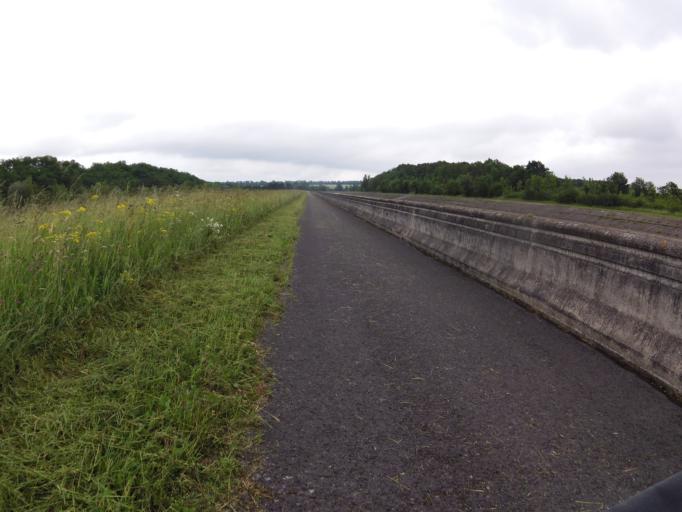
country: FR
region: Champagne-Ardenne
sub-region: Departement de la Haute-Marne
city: Villiers-en-Lieu
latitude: 48.6077
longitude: 4.8638
